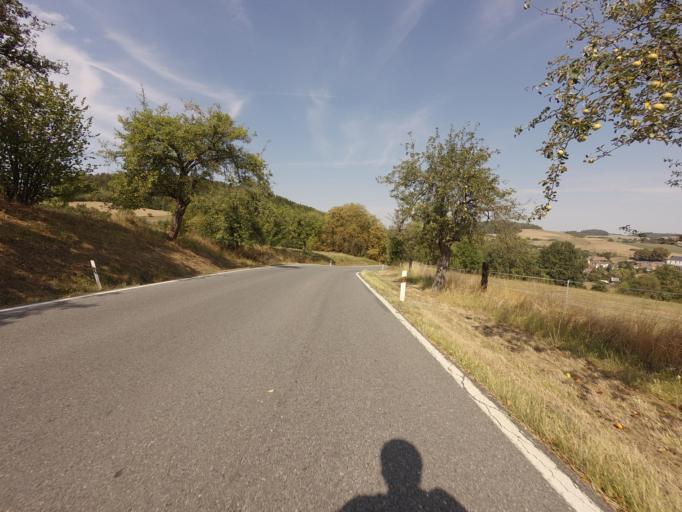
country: CZ
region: Central Bohemia
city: Petrovice
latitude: 49.5911
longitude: 14.3805
